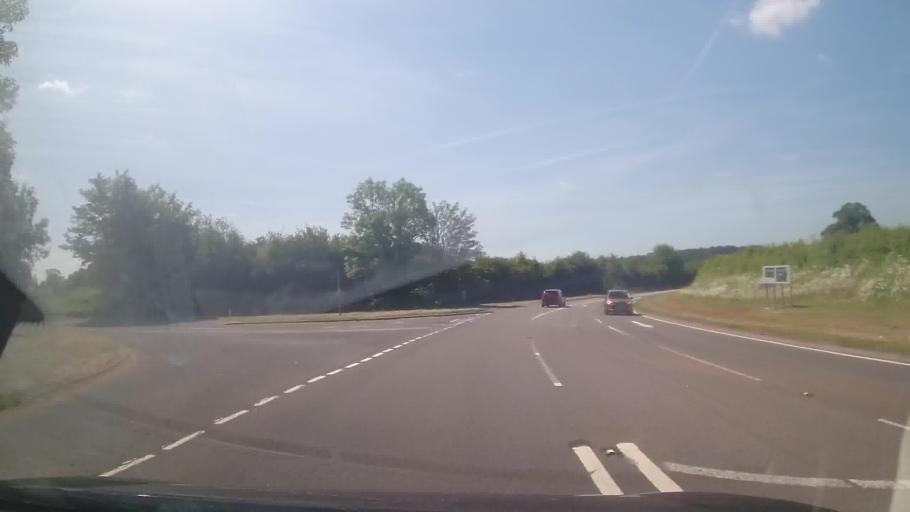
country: GB
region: England
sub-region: Herefordshire
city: Kimbolton
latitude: 52.2445
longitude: -2.7144
